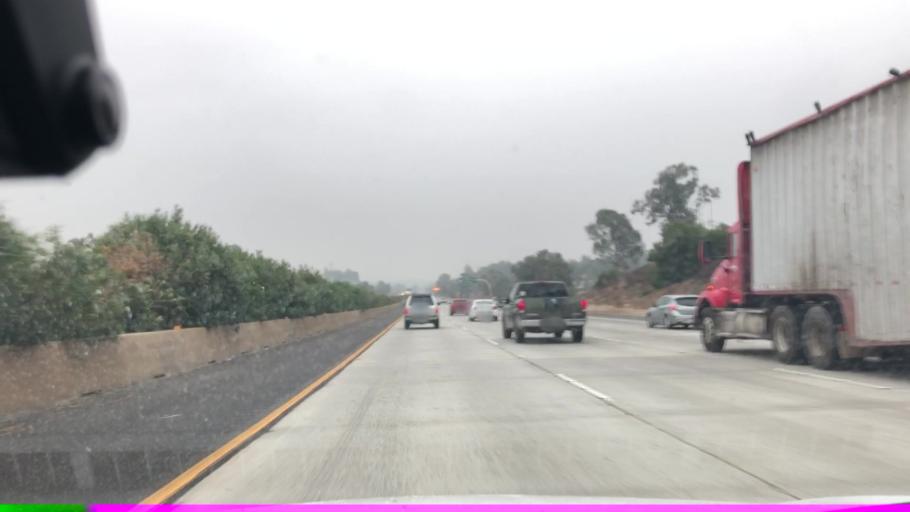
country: US
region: California
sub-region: San Diego County
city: Escondido
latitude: 33.1535
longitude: -117.1042
